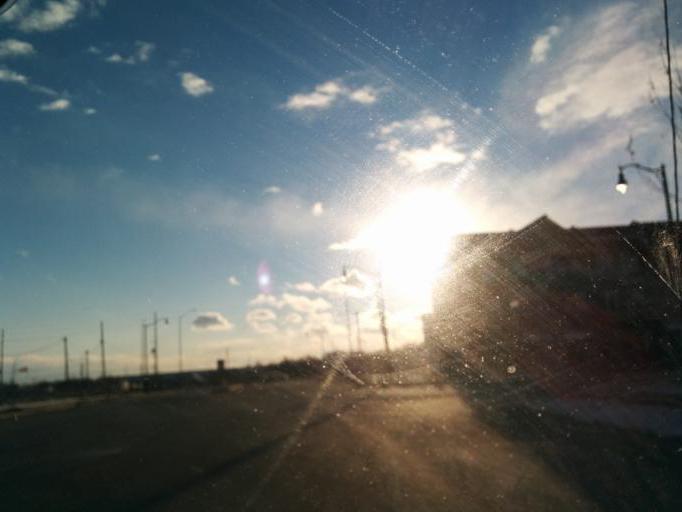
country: CA
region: Ontario
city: Brampton
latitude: 43.6307
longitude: -79.7776
